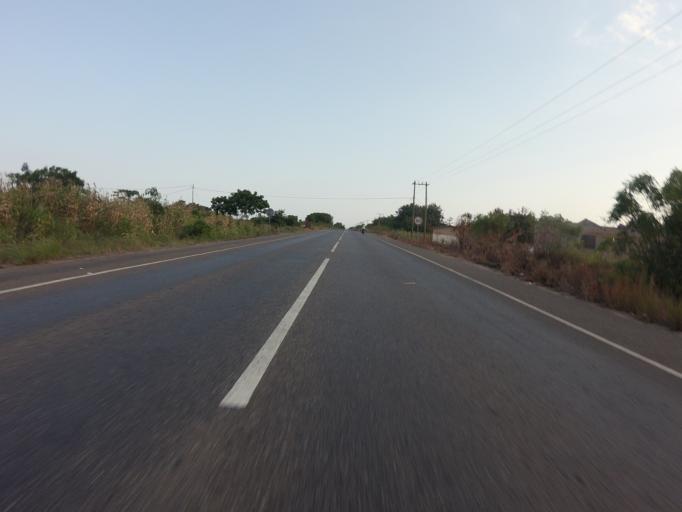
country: GH
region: Volta
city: Anloga
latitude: 6.0657
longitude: 0.6045
